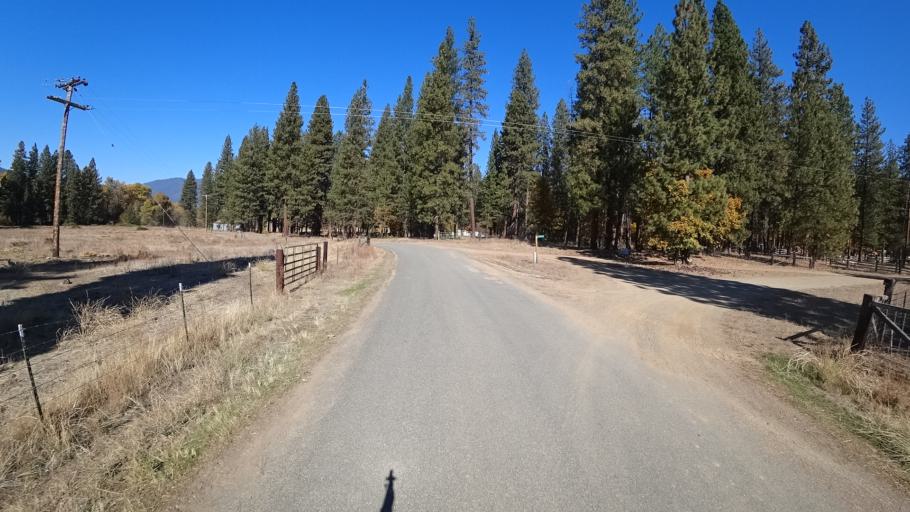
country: US
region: California
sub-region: Siskiyou County
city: Yreka
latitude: 41.6015
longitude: -122.9573
